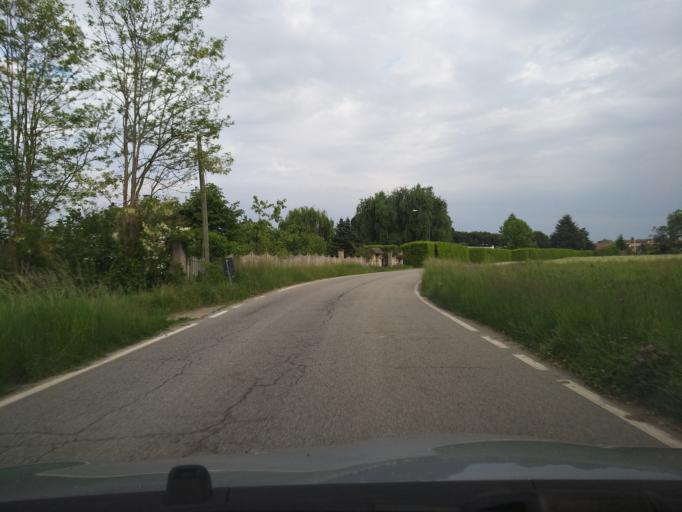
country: IT
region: Piedmont
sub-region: Provincia di Torino
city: Roletto
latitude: 44.9096
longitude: 7.3502
